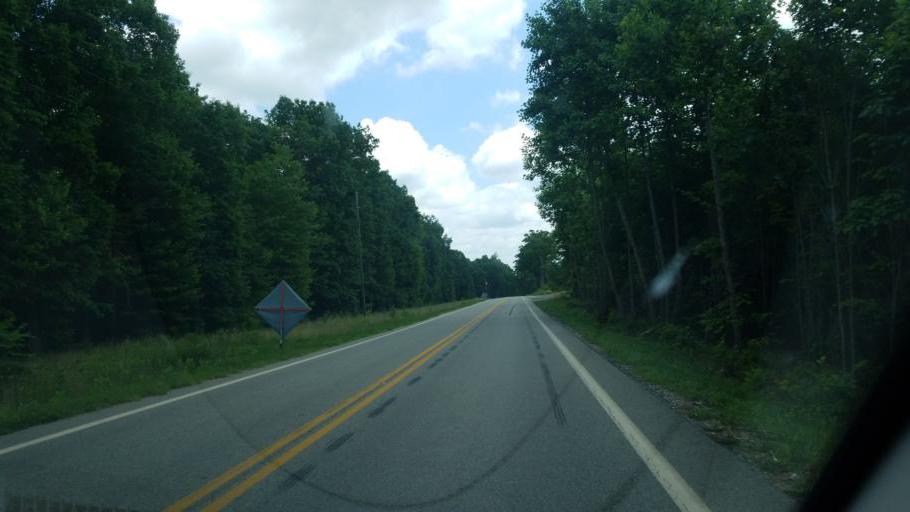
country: US
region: Virginia
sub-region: Buckingham County
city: Buckingham
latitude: 37.5307
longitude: -78.7092
